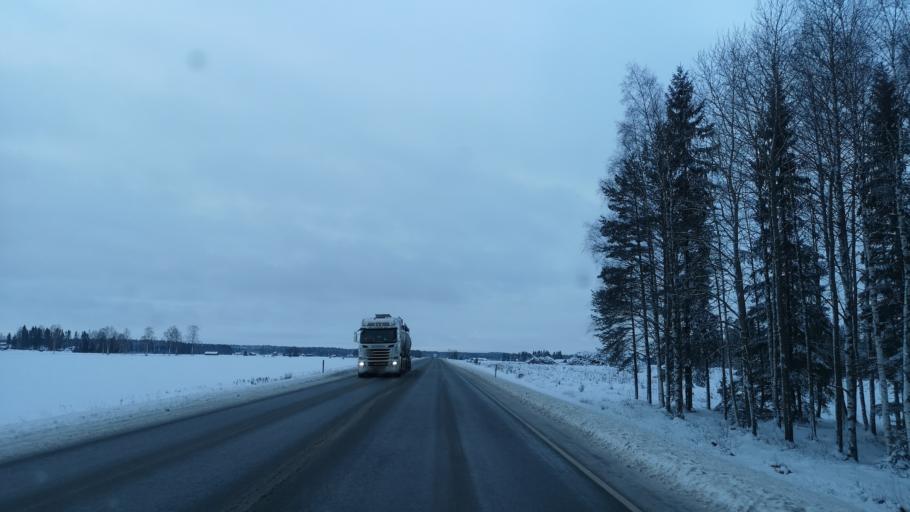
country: FI
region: Varsinais-Suomi
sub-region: Loimaa
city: Loimaa
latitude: 60.8935
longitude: 23.1138
